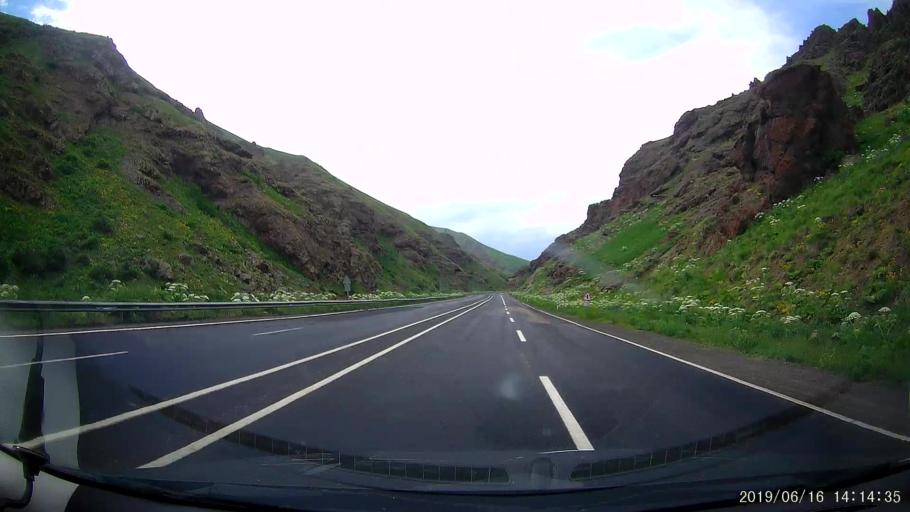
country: TR
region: Agri
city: Tahir
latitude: 39.7964
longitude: 42.4943
